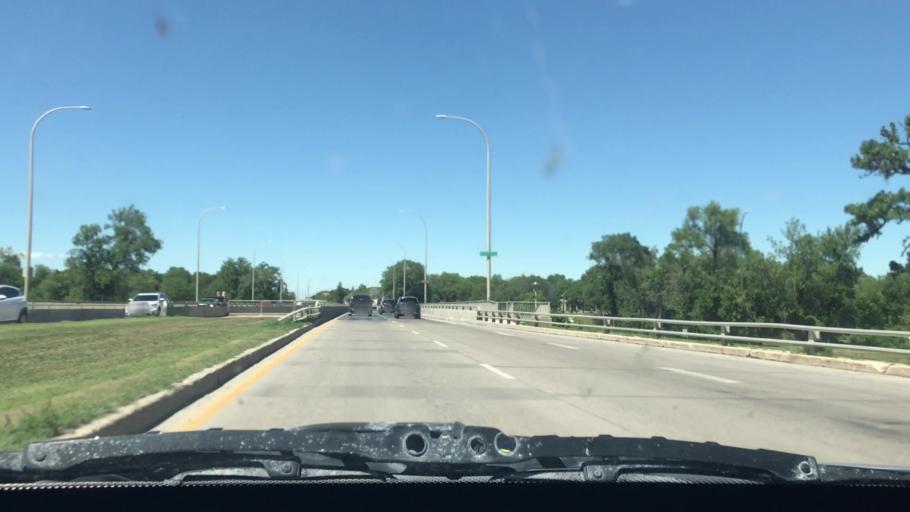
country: CA
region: Manitoba
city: Winnipeg
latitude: 49.8540
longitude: -97.1256
